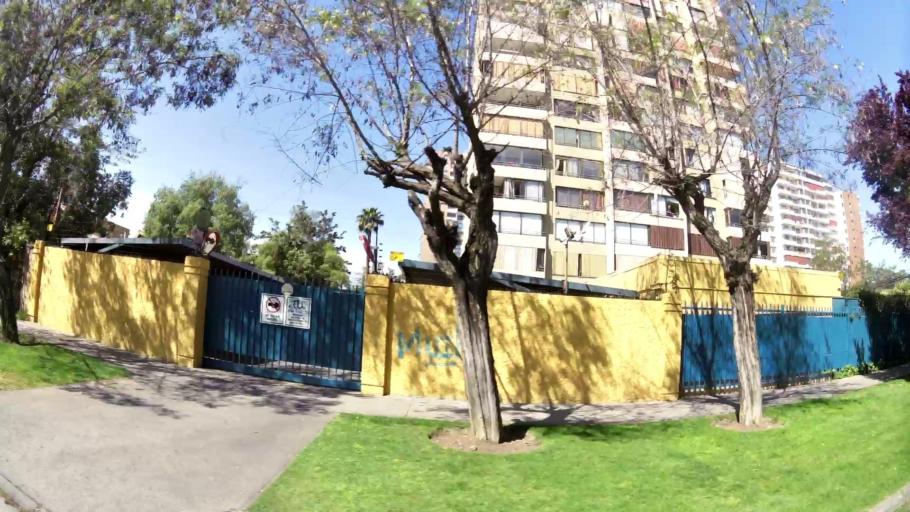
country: CL
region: Santiago Metropolitan
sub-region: Provincia de Santiago
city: Santiago
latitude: -33.5076
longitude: -70.6537
